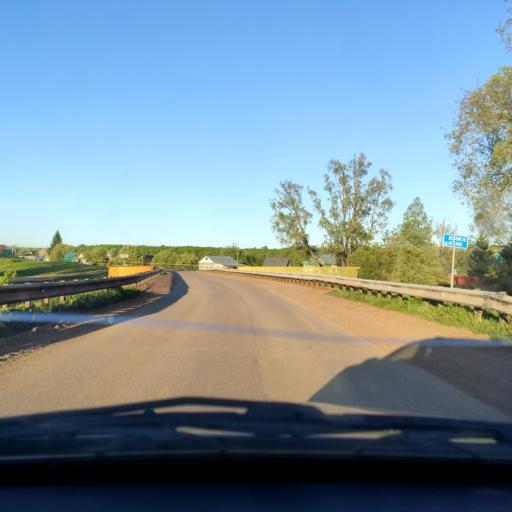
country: RU
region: Bashkortostan
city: Yazykovo
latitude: 55.0253
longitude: 56.2141
